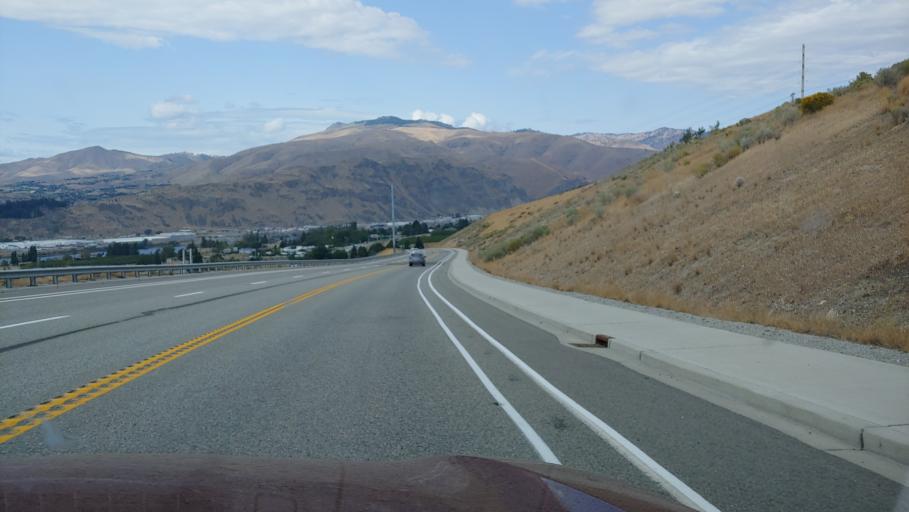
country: US
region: Washington
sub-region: Douglas County
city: East Wenatchee Bench
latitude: 47.4613
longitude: -120.2928
